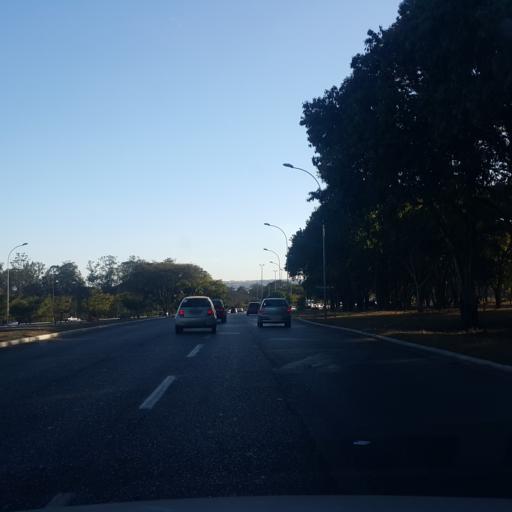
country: BR
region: Federal District
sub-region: Brasilia
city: Brasilia
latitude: -15.8436
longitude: -47.9327
